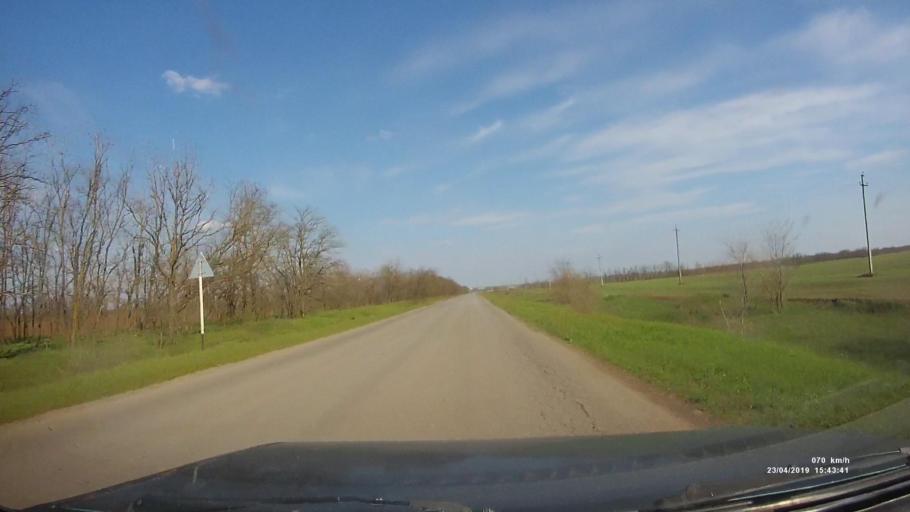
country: RU
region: Rostov
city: Remontnoye
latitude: 46.5441
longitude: 43.0861
